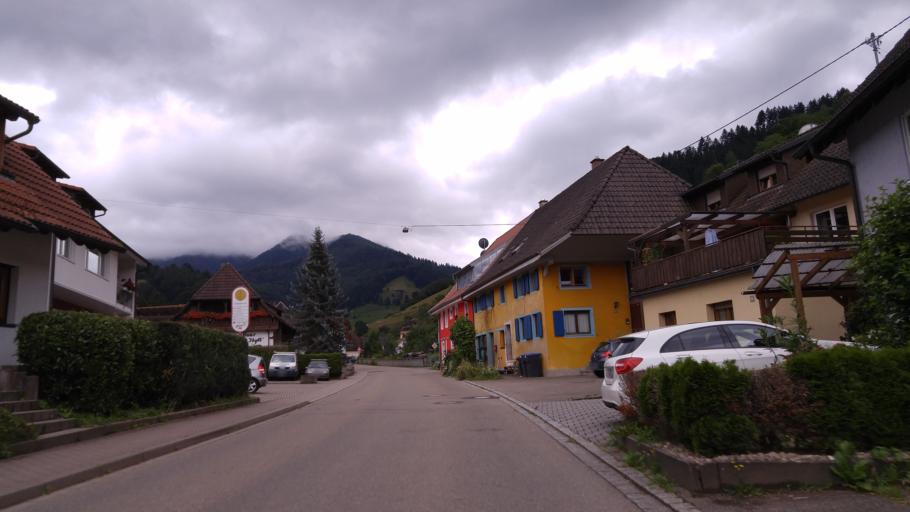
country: DE
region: Baden-Wuerttemberg
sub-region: Freiburg Region
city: Muenstertal/Schwarzwald
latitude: 47.8517
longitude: 7.7871
